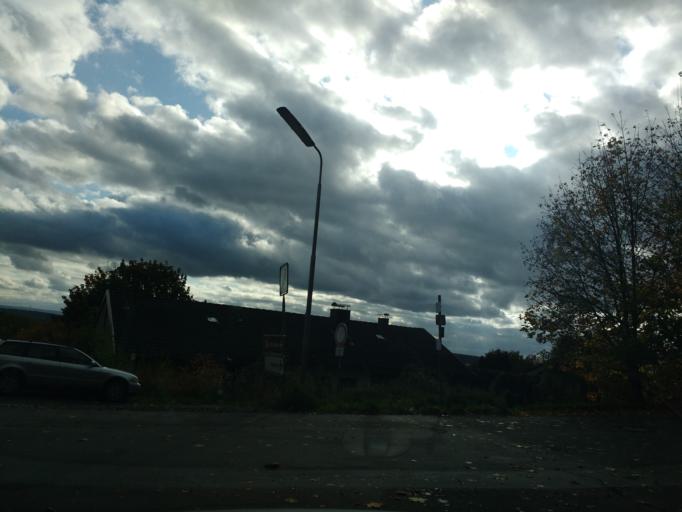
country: DE
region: Lower Saxony
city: Herzberg am Harz
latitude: 51.6519
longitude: 10.3295
